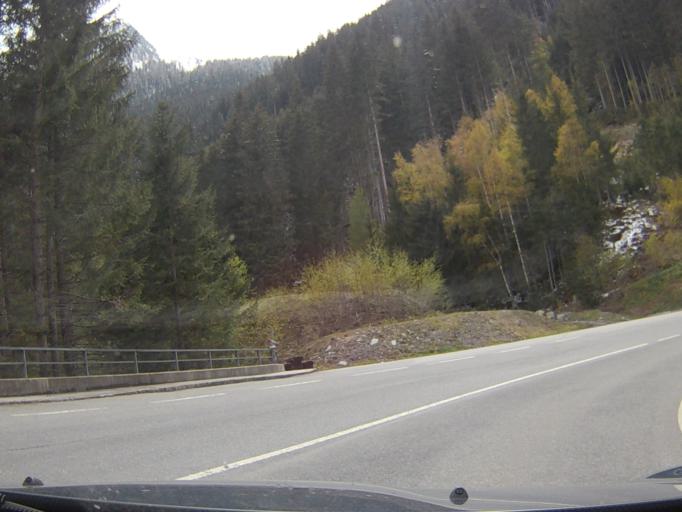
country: AT
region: Salzburg
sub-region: Politischer Bezirk Zell am See
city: Krimml
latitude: 47.2123
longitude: 12.1660
